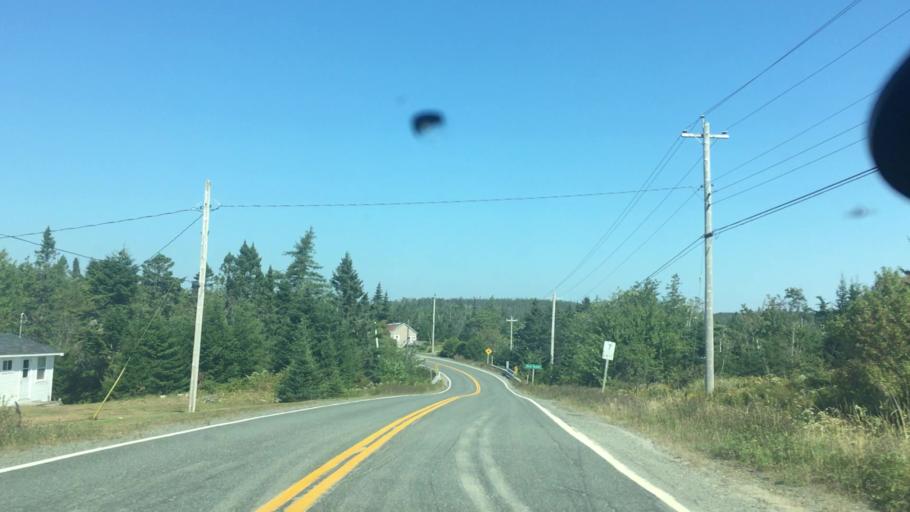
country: CA
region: Nova Scotia
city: Antigonish
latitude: 44.9987
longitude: -62.0997
